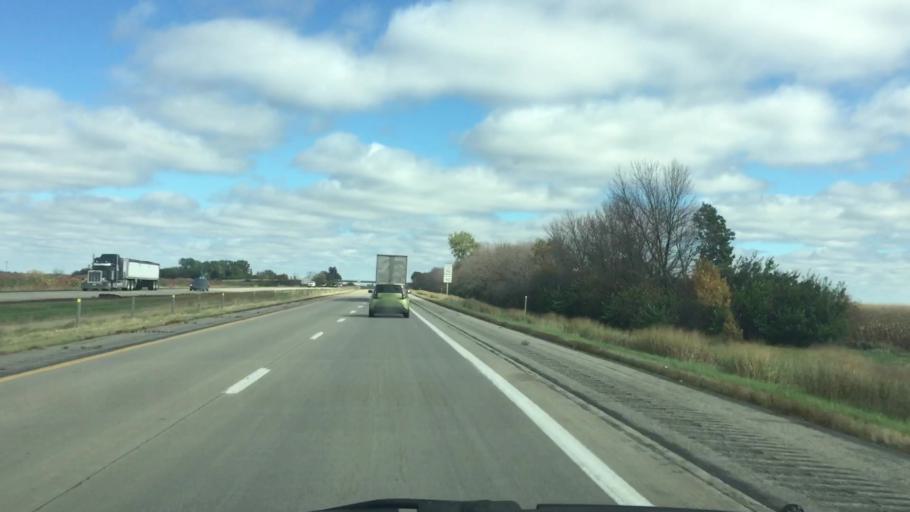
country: US
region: Iowa
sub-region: Jasper County
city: Newton
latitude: 41.6839
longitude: -92.8903
